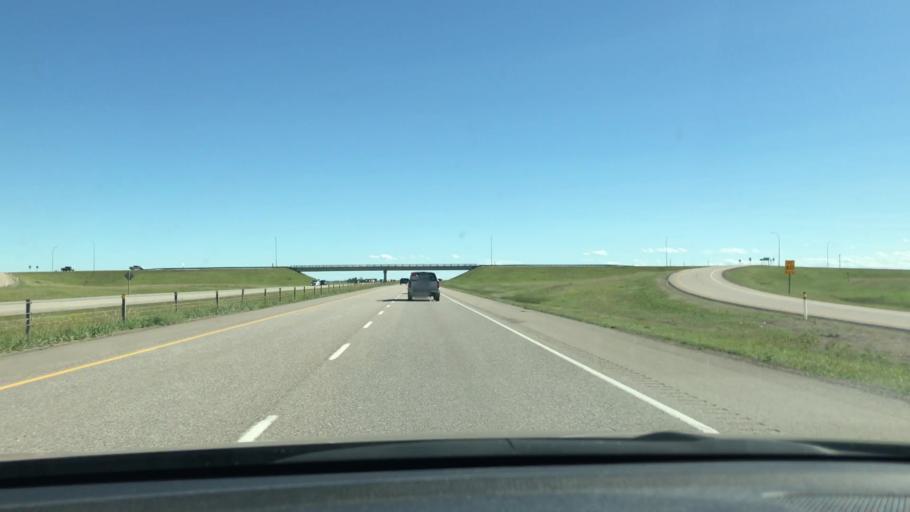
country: CA
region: Alberta
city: Didsbury
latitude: 51.6672
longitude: -114.0257
